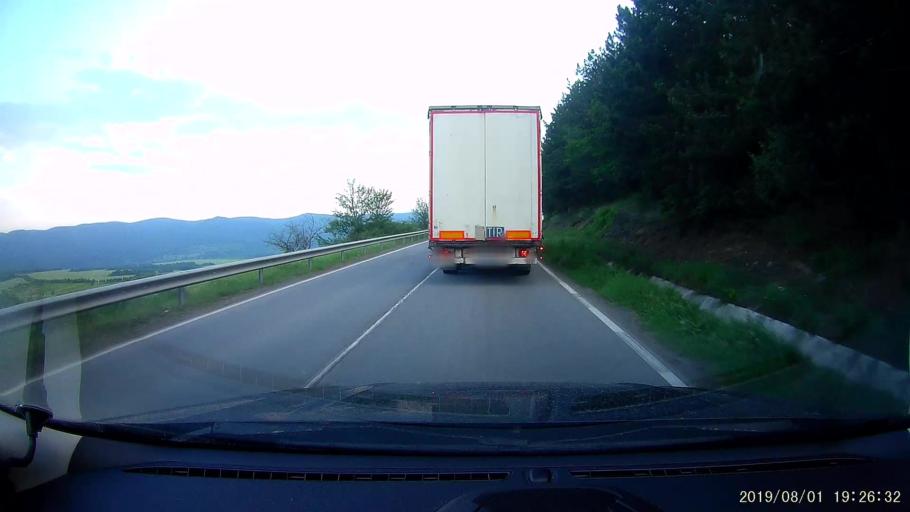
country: BG
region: Burgas
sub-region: Obshtina Sungurlare
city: Sungurlare
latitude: 42.8565
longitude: 26.9399
